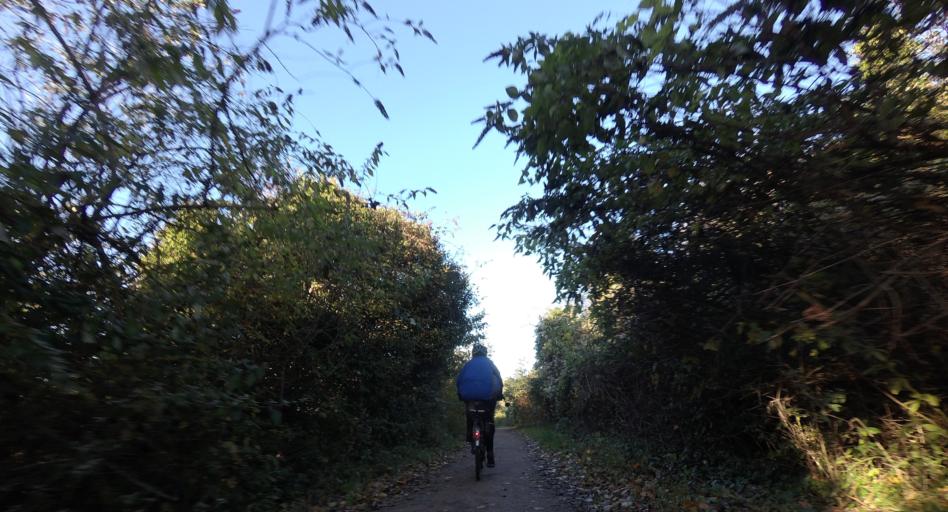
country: GB
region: England
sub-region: West Sussex
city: Steyning
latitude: 50.8663
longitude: -0.2981
